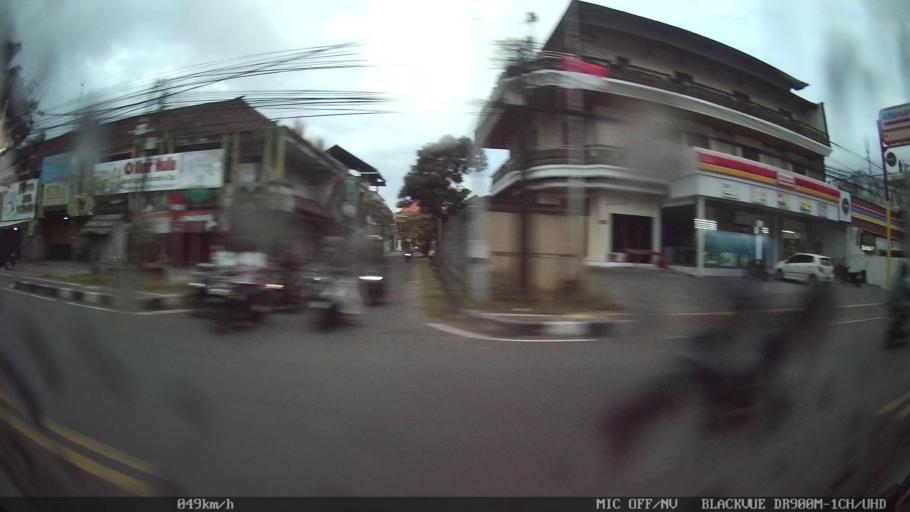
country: ID
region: Bali
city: Banjar Kayangan
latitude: -8.6354
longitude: 115.2262
